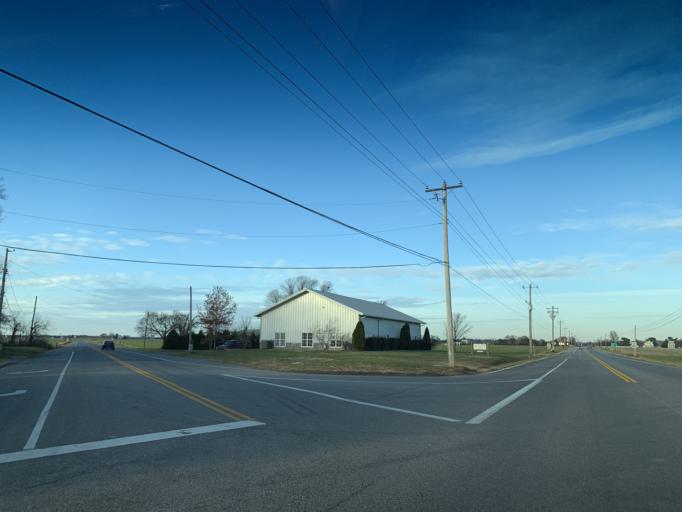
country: US
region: Maryland
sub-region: Kent County
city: Chestertown
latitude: 39.2394
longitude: -76.0669
